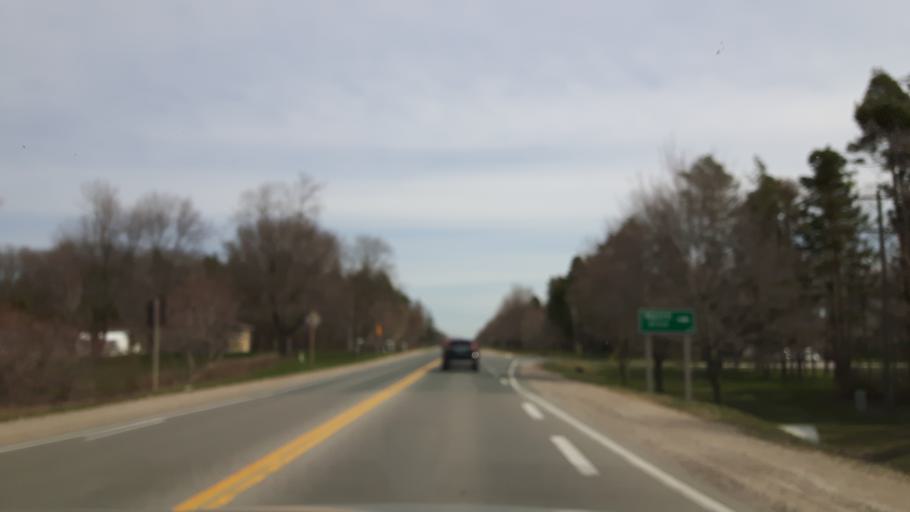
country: CA
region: Ontario
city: Goderich
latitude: 43.7281
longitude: -81.6864
